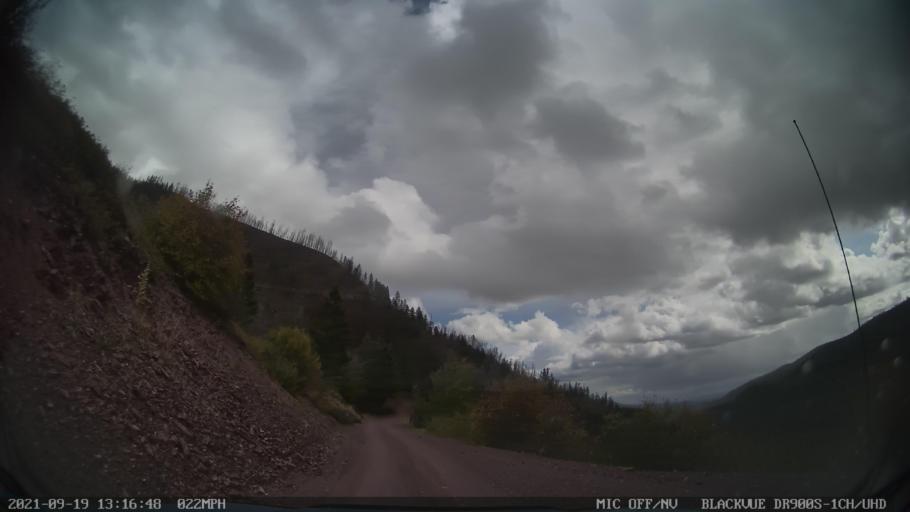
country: US
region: Montana
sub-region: Missoula County
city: Seeley Lake
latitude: 47.1763
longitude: -113.3676
